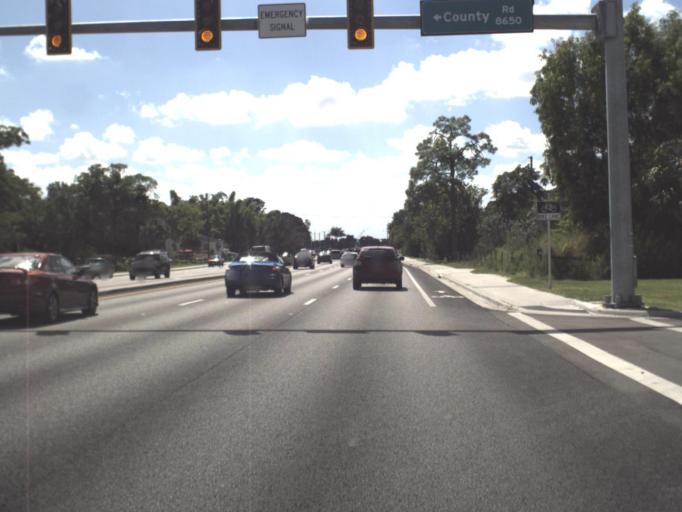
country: US
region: Florida
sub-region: Lee County
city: Estero
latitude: 26.4372
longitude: -81.8110
